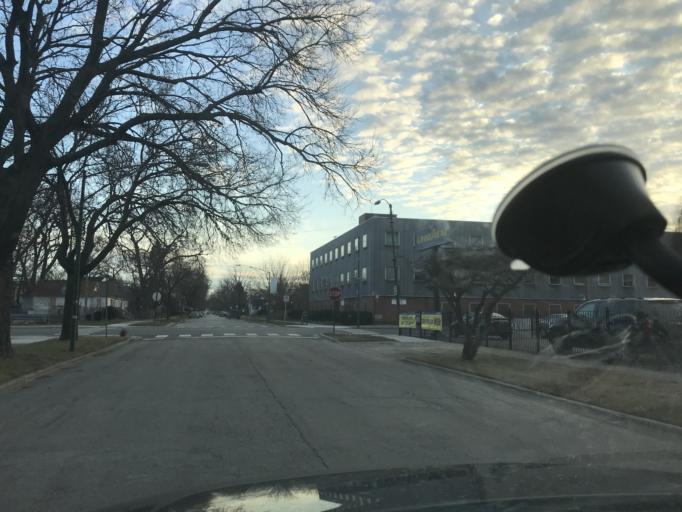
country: US
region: Illinois
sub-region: Cook County
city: Burnham
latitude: 41.7374
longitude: -87.5793
